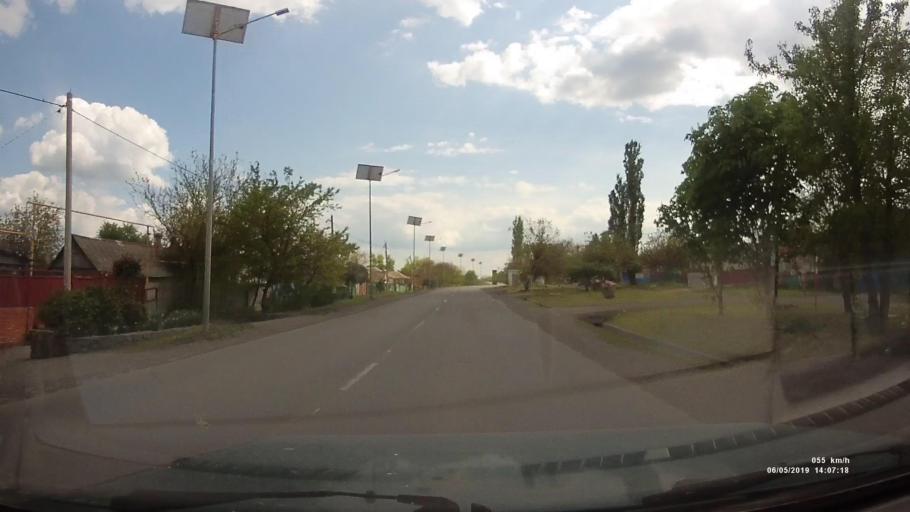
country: RU
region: Rostov
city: Shakhty
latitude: 47.6821
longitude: 40.3032
